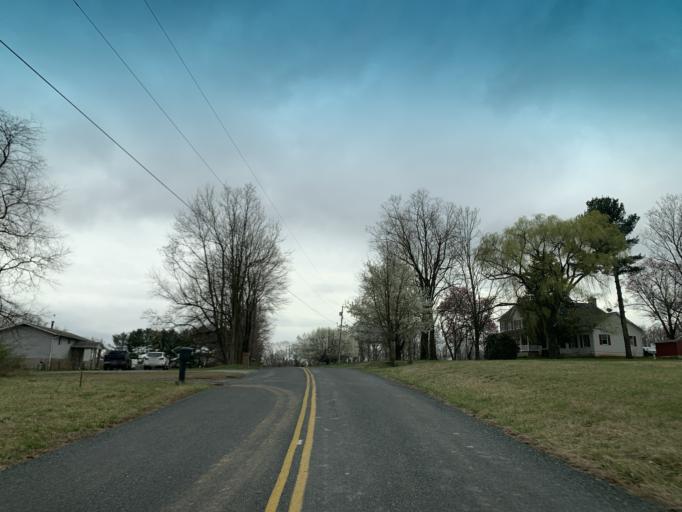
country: US
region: Maryland
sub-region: Harford County
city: Aberdeen
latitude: 39.5267
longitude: -76.2095
